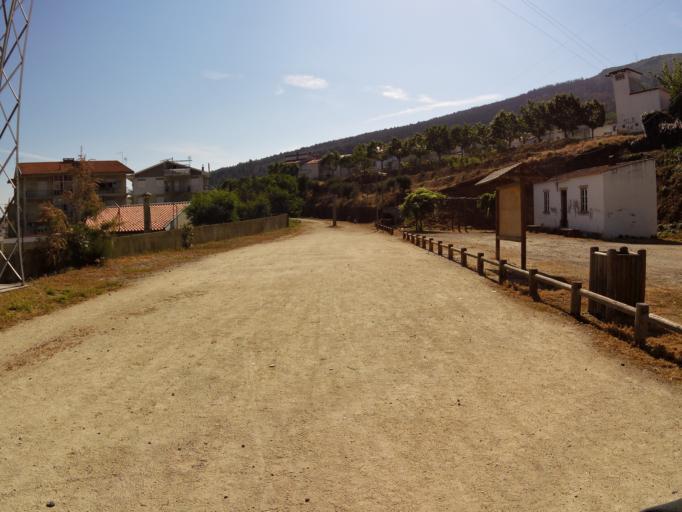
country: PT
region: Braganca
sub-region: Torre de Moncorvo
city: Torre de Moncorvo
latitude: 41.1723
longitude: -7.0492
